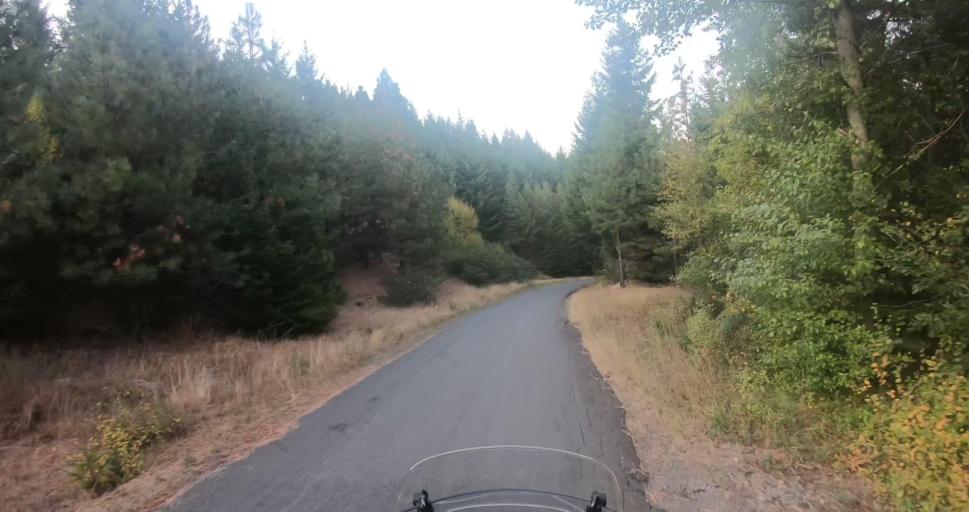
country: US
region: Oregon
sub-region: Hood River County
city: Odell
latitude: 45.4687
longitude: -121.6152
